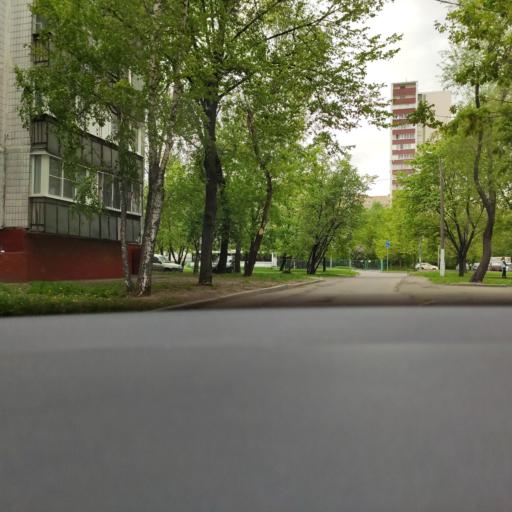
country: RU
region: Moscow
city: Otradnoye
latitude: 55.8699
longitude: 37.6062
